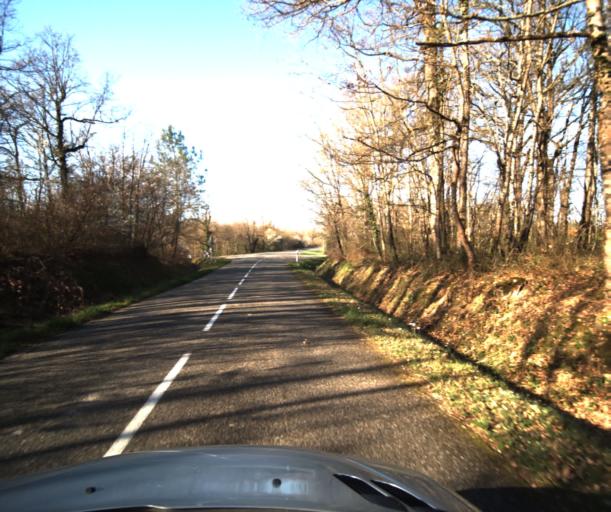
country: FR
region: Midi-Pyrenees
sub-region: Departement du Tarn-et-Garonne
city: Campsas
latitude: 43.9348
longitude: 1.2970
